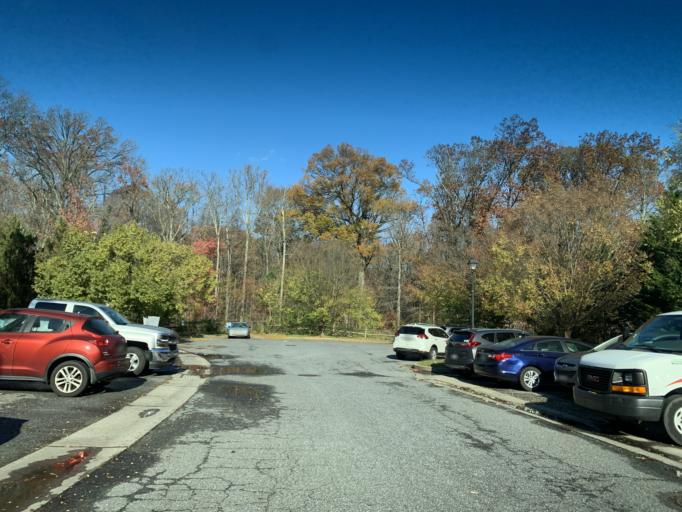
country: US
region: Maryland
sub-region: Baltimore County
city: Middle River
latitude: 39.3544
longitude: -76.4412
